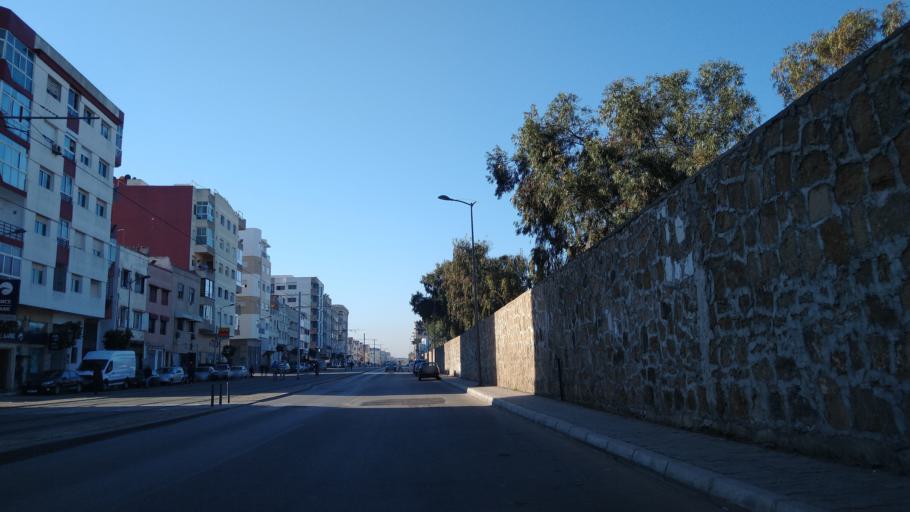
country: MA
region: Rabat-Sale-Zemmour-Zaer
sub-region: Rabat
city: Rabat
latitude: 34.0143
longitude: -6.8564
